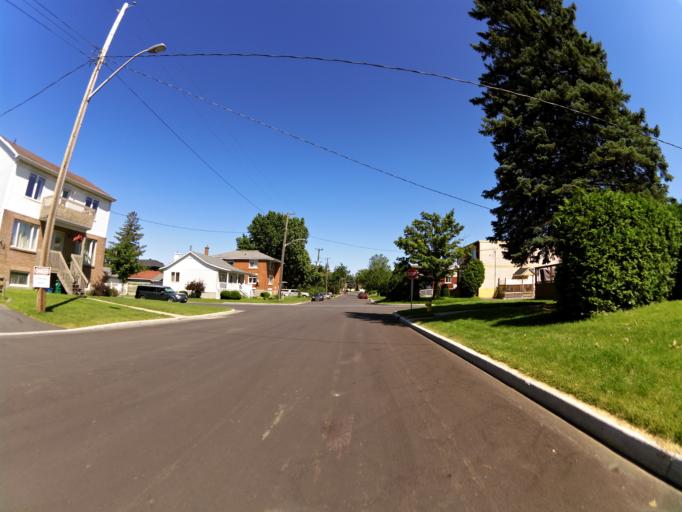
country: CA
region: Ontario
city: Ottawa
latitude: 45.4267
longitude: -75.6555
